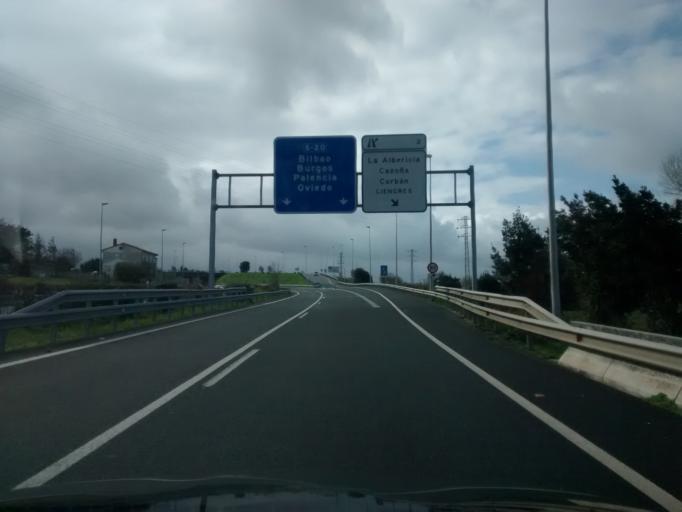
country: ES
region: Cantabria
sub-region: Provincia de Cantabria
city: Santa Cruz de Bezana
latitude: 43.4623
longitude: -3.8584
